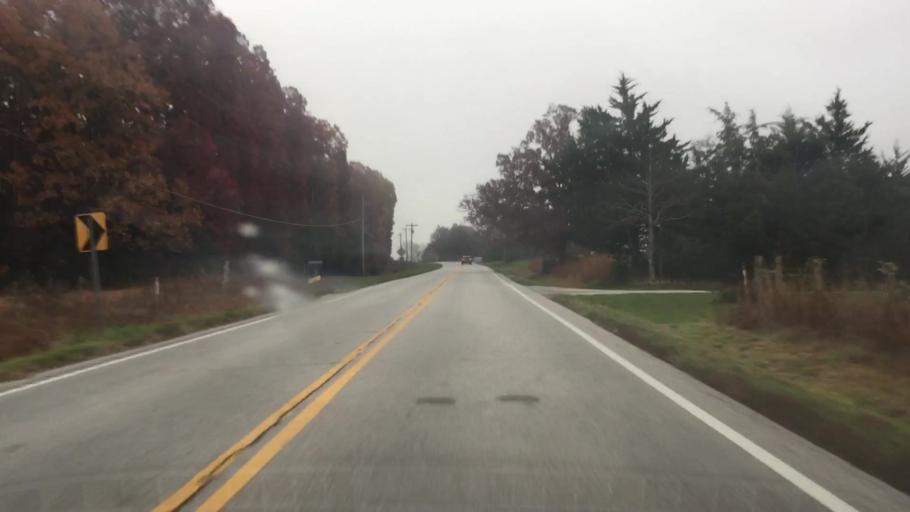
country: US
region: Missouri
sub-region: Callaway County
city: Fulton
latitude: 38.8764
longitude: -92.0731
